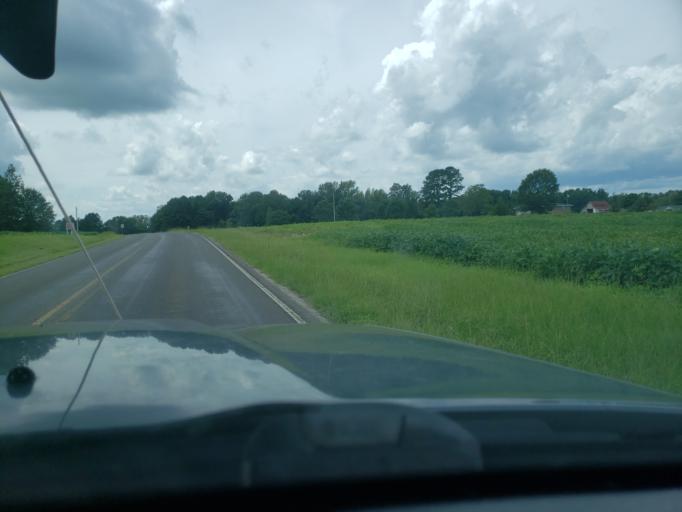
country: US
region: North Carolina
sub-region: Wake County
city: Zebulon
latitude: 35.8867
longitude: -78.3458
